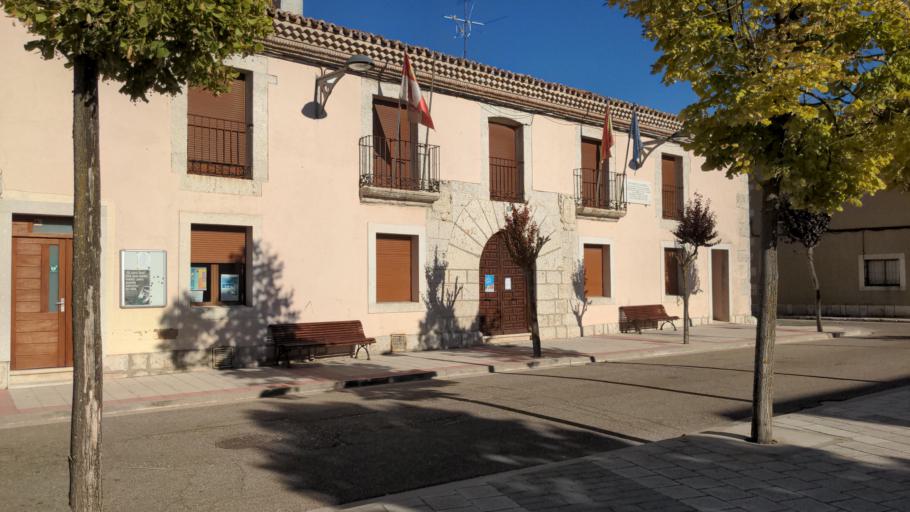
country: ES
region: Castille and Leon
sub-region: Provincia de Valladolid
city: Tudela de Duero
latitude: 41.5371
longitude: -4.5343
